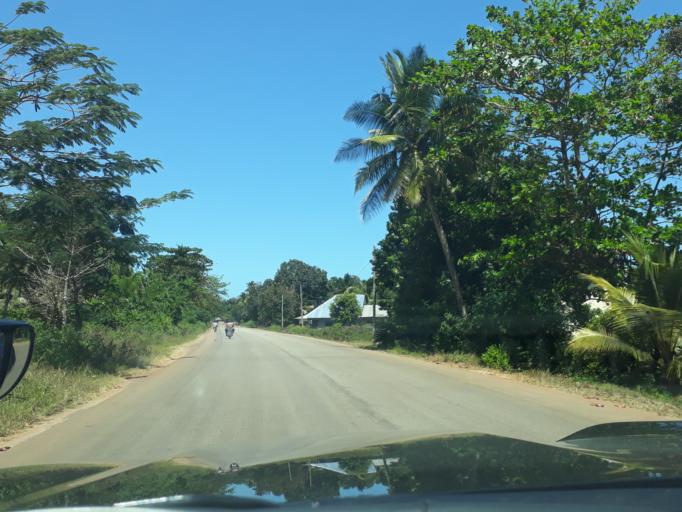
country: TZ
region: Zanzibar Urban/West
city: Zanzibar
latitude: -6.2657
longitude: 39.2637
